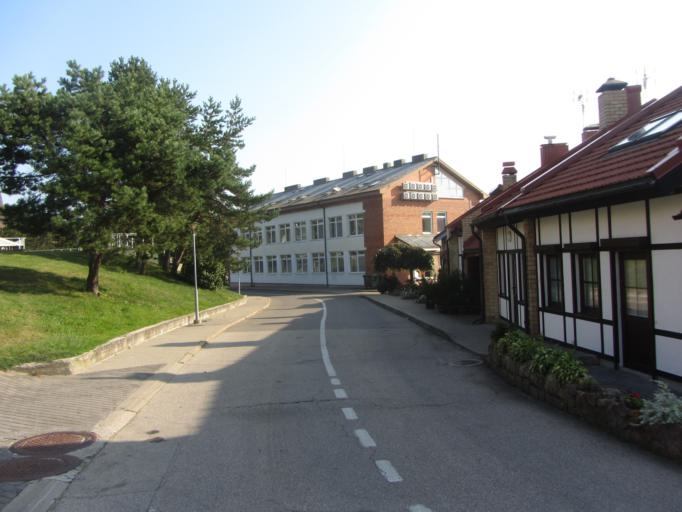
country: LT
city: Nida
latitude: 55.3021
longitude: 21.0014
